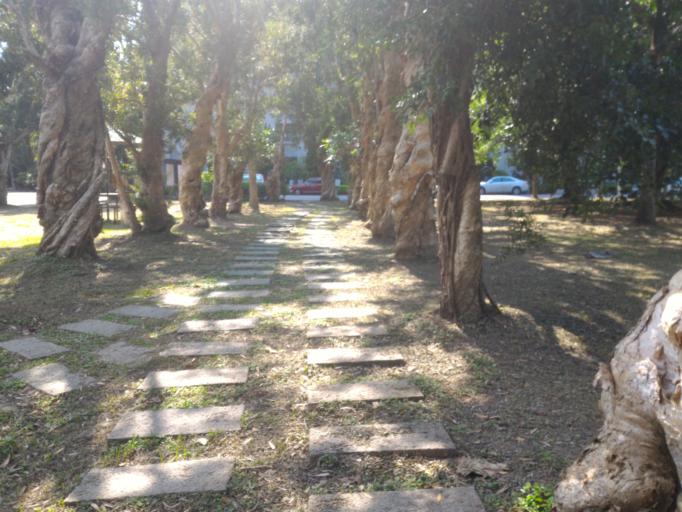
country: TW
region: Taipei
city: Taipei
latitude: 25.0415
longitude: 121.6165
